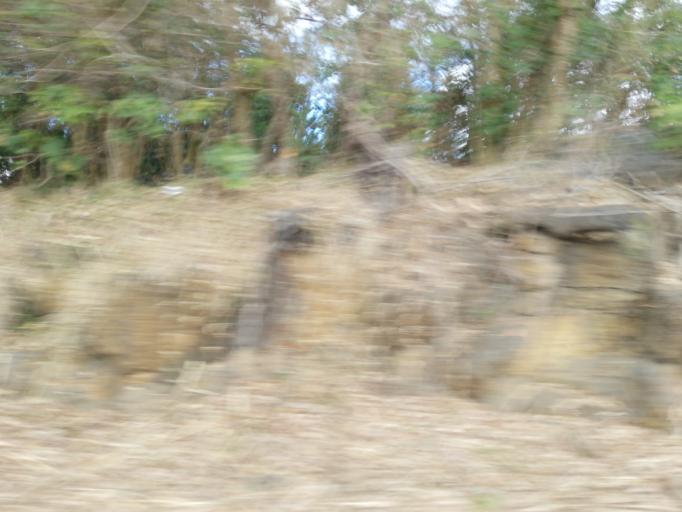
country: MU
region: Flacq
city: Grande Riviere Sud Est
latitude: -20.2739
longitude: 57.7686
